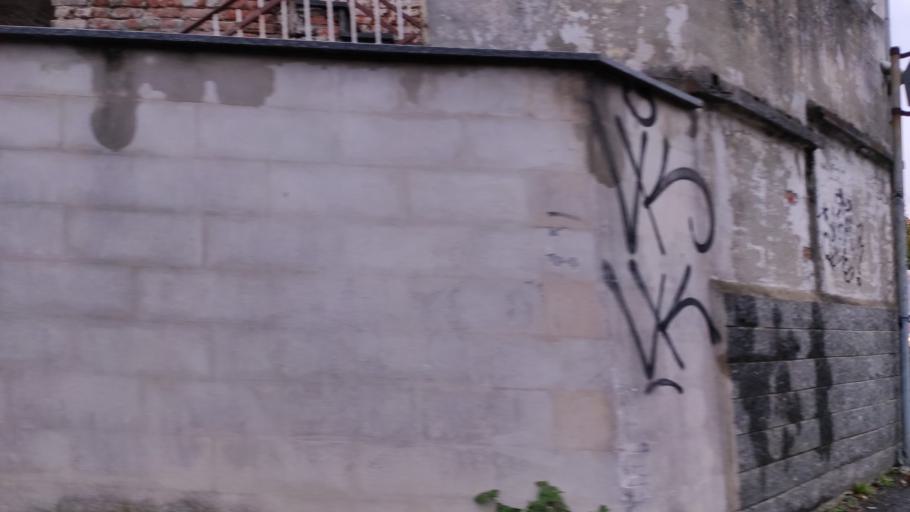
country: IT
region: Piedmont
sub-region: Provincia di Torino
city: Settimo Torinese
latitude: 45.1435
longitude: 7.7679
